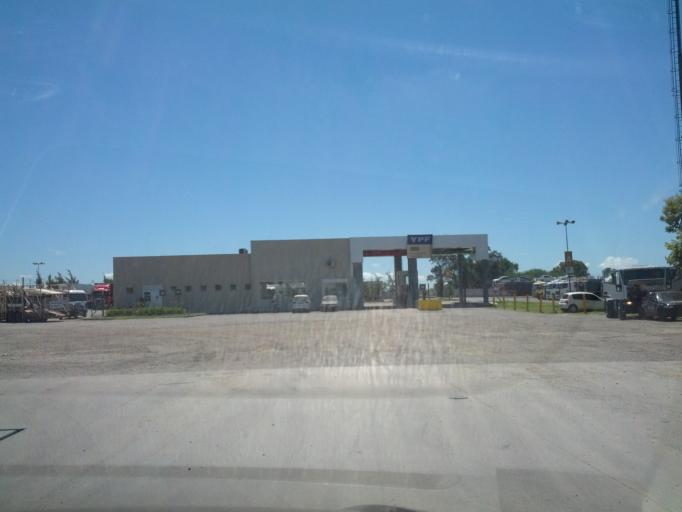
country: AR
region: Buenos Aires
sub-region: Partido de Zarate
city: Zarate
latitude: -34.1348
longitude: -59.0466
